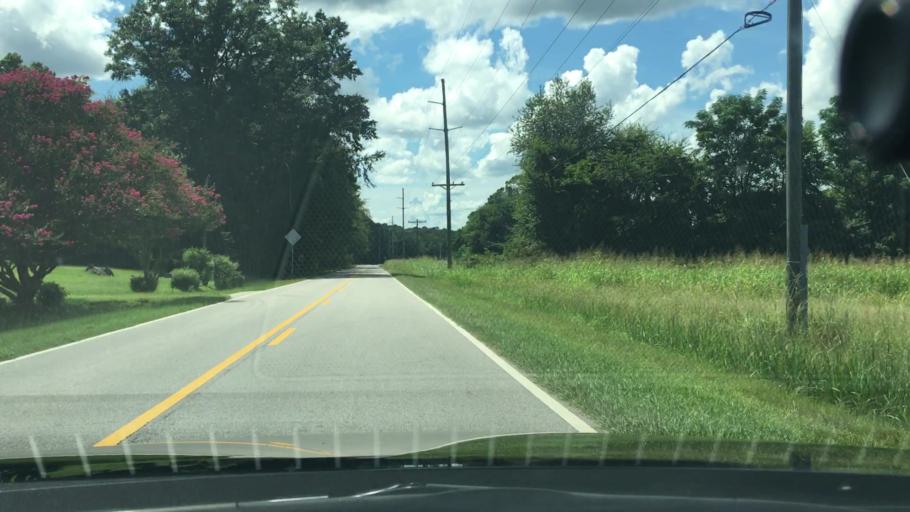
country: US
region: Georgia
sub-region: Putnam County
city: Jefferson
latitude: 33.3663
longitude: -83.2785
